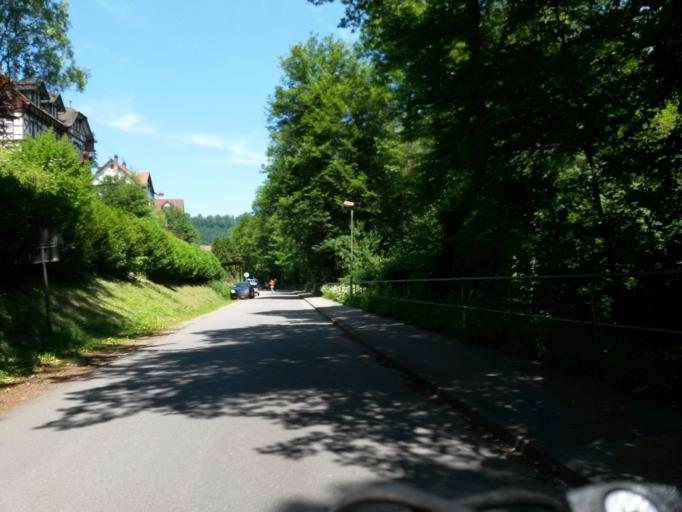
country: DE
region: Baden-Wuerttemberg
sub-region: Karlsruhe Region
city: Calw
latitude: 48.7069
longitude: 8.7374
